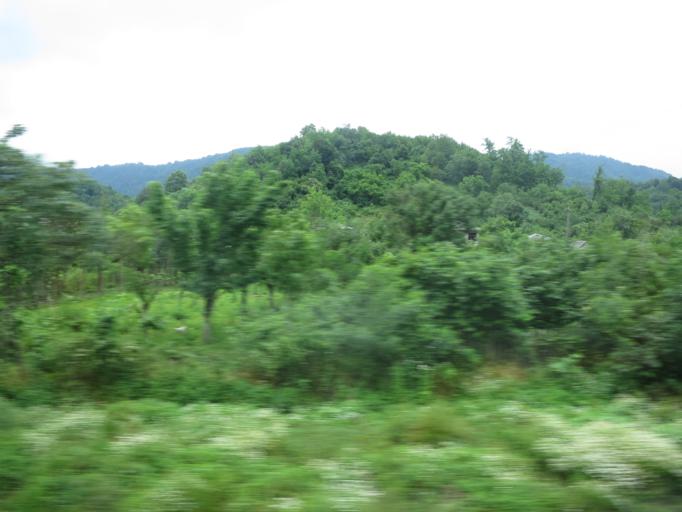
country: GE
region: Samegrelo and Zemo Svaneti
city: Abasha
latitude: 42.0952
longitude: 42.1855
